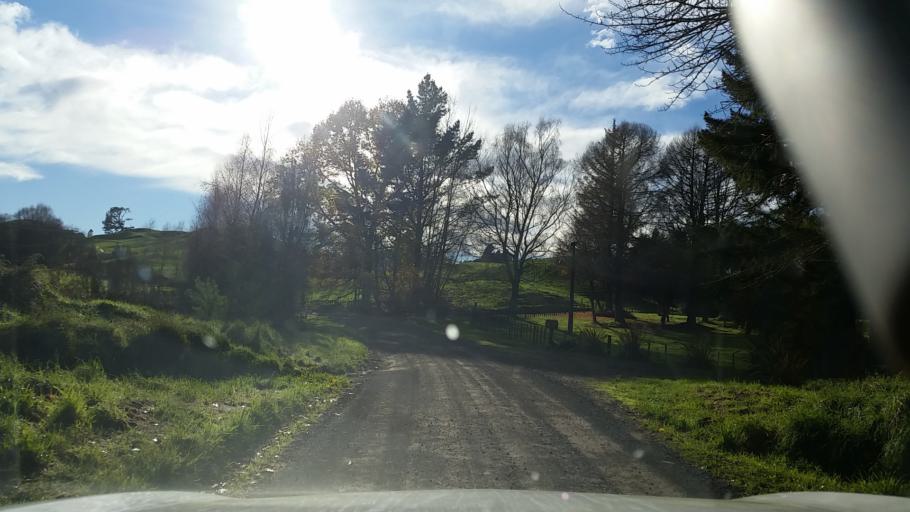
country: NZ
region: Waikato
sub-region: South Waikato District
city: Tokoroa
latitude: -38.3798
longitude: 176.0856
